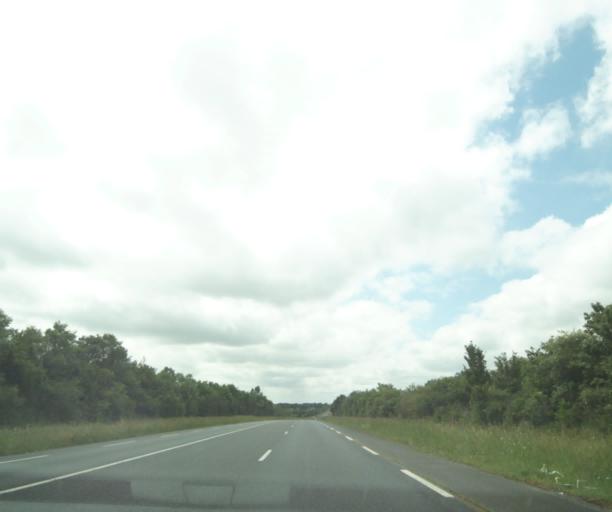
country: FR
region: Poitou-Charentes
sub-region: Departement des Deux-Sevres
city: Airvault
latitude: 46.7930
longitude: -0.2140
